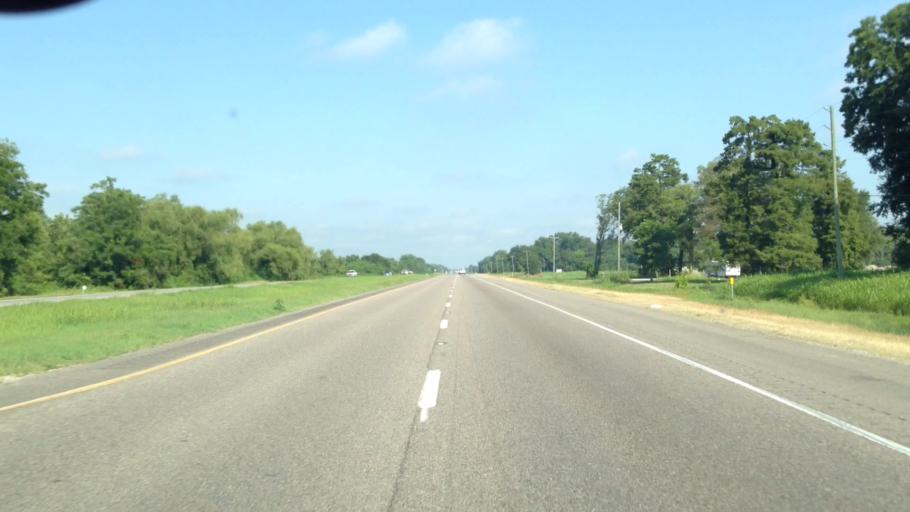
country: US
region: Louisiana
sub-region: West Baton Rouge Parish
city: Erwinville
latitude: 30.5128
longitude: -91.3466
